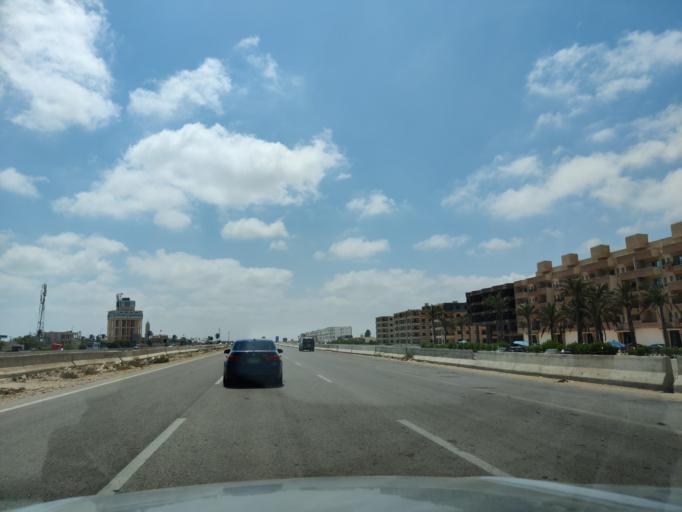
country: EG
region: Muhafazat Matruh
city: Al `Alamayn
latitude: 30.8184
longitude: 29.0253
